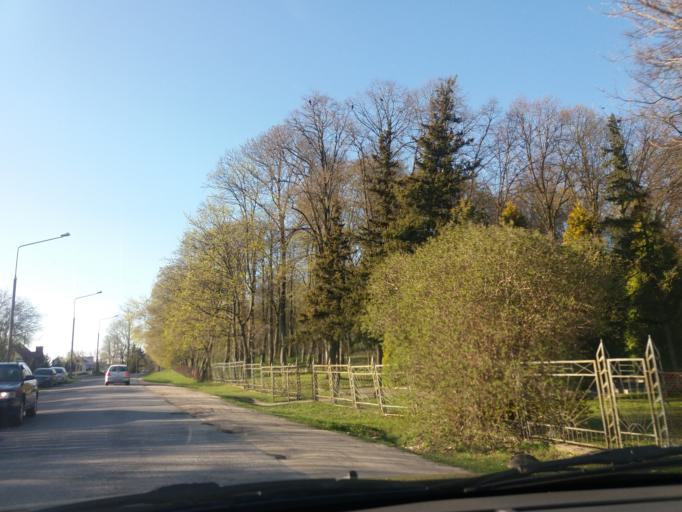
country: PL
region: Warmian-Masurian Voivodeship
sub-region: Powiat nidzicki
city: Nidzica
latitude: 53.3491
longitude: 20.4304
